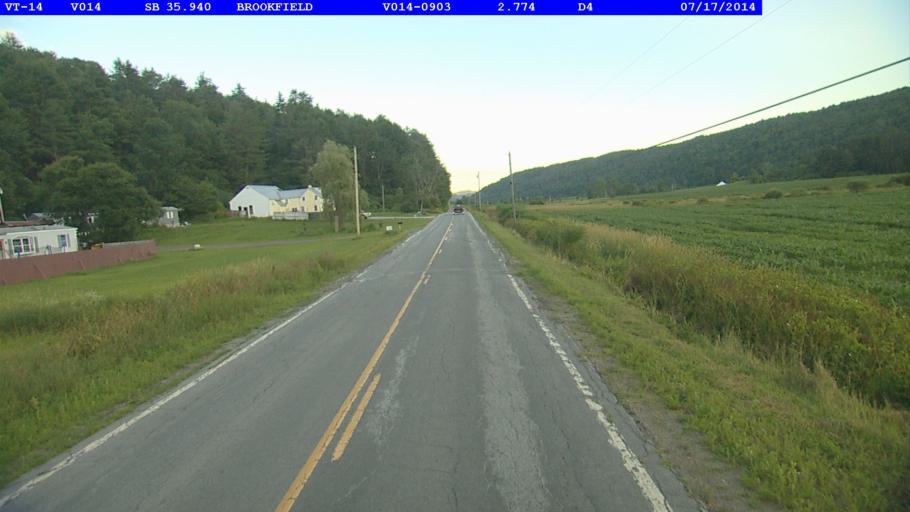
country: US
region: Vermont
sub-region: Orange County
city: Williamstown
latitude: 44.0169
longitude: -72.5698
